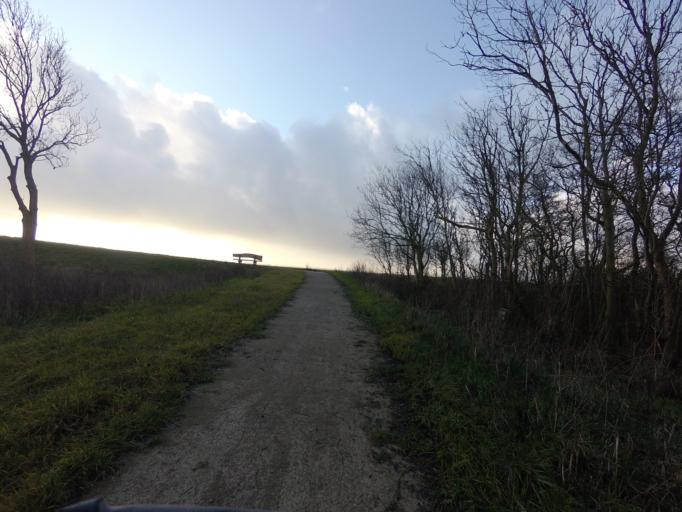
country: NL
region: North Holland
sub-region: Gemeente Texel
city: Den Burg
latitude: 53.0931
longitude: 4.8077
